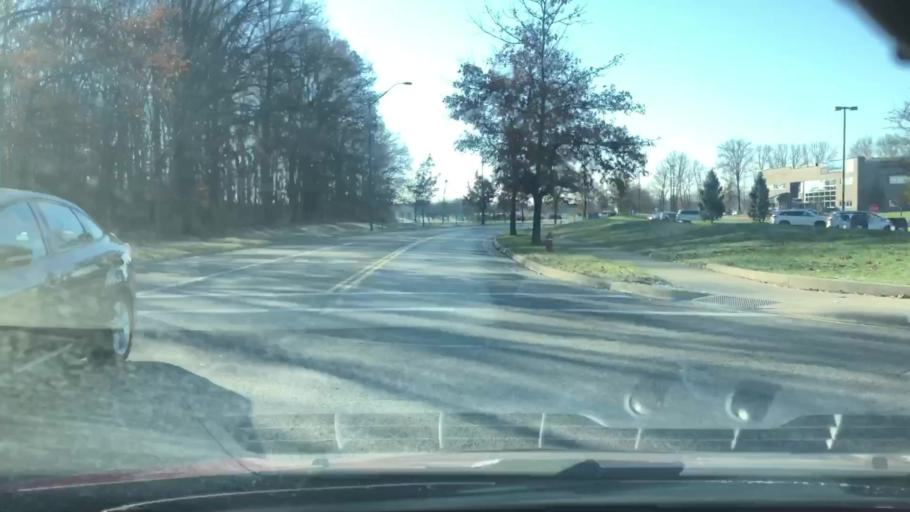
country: US
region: Ohio
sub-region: Franklin County
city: Westerville
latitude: 40.1419
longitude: -82.9202
